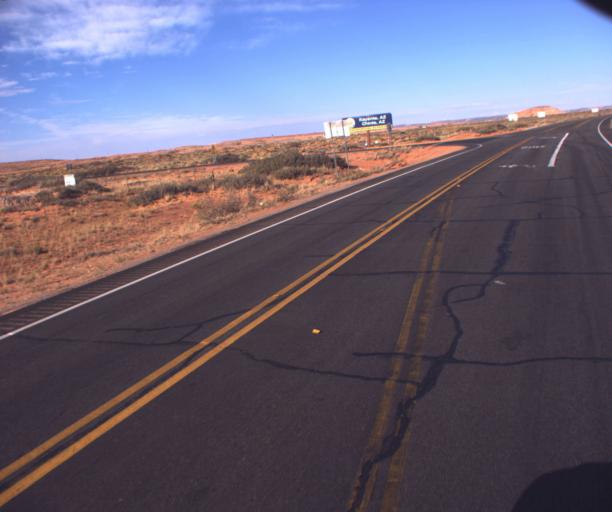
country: US
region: Arizona
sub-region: Apache County
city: Many Farms
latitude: 36.9250
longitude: -109.6140
